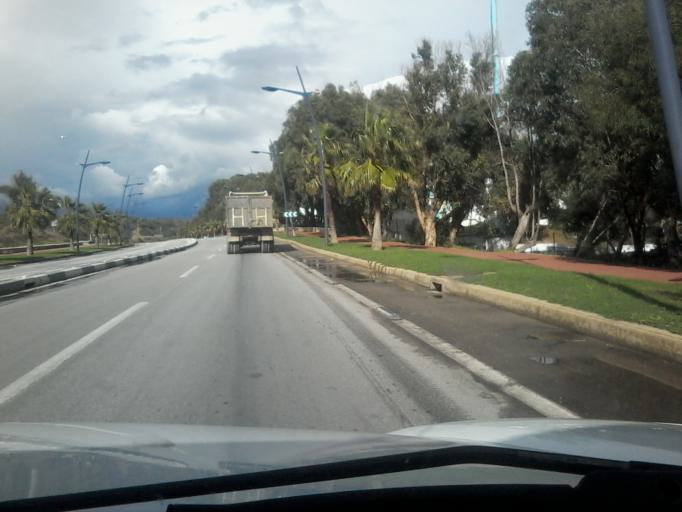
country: ES
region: Ceuta
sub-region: Ceuta
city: Ceuta
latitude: 35.7656
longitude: -5.3486
